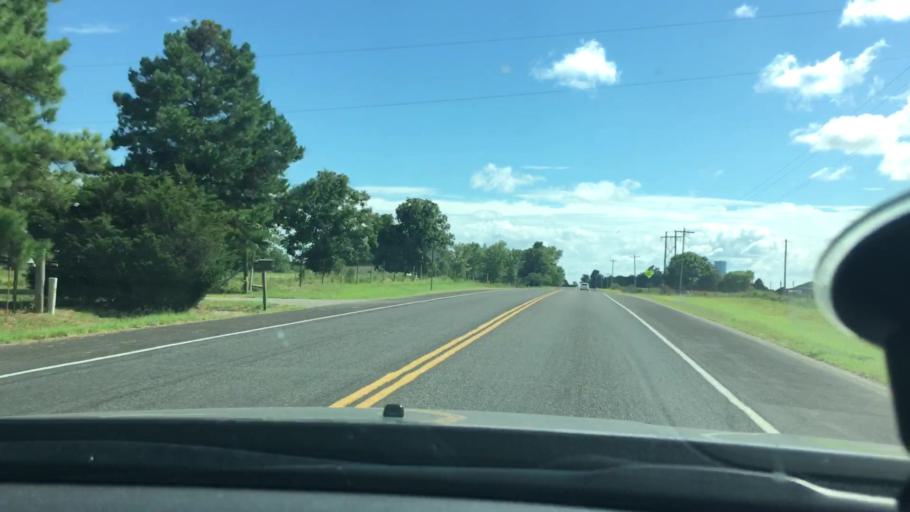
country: US
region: Oklahoma
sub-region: Sequoyah County
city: Vian
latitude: 35.5728
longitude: -94.9853
